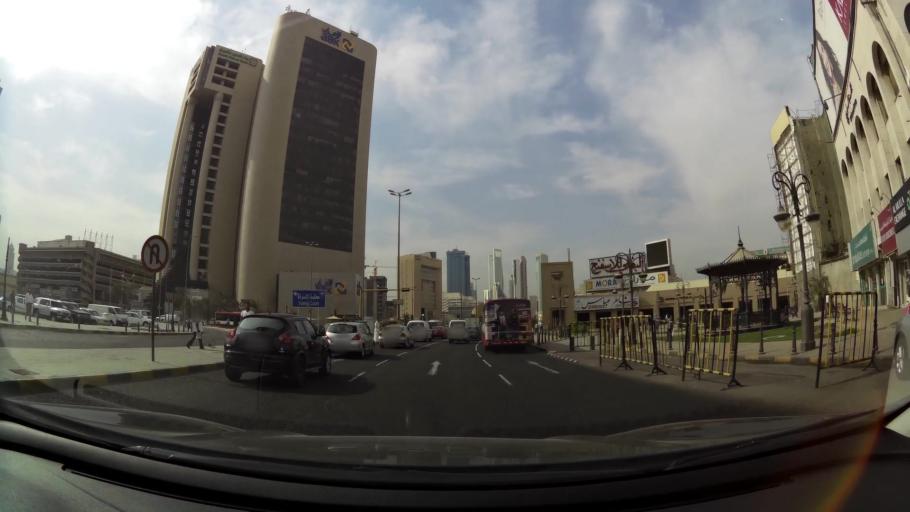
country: KW
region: Al Asimah
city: Kuwait City
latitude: 29.3734
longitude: 47.9758
